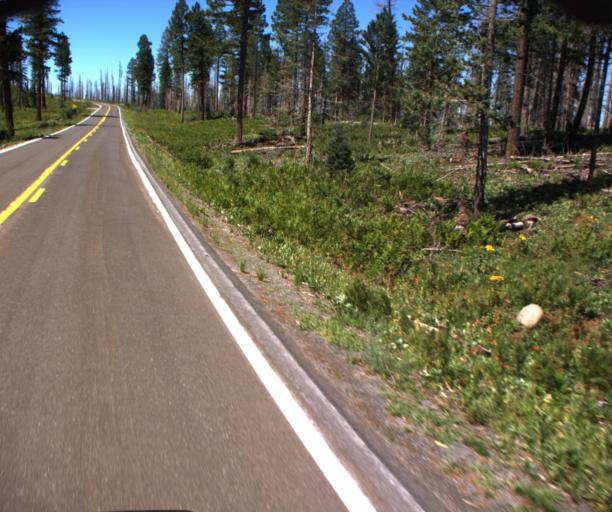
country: US
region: Arizona
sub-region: Apache County
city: Eagar
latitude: 33.5980
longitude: -109.3466
